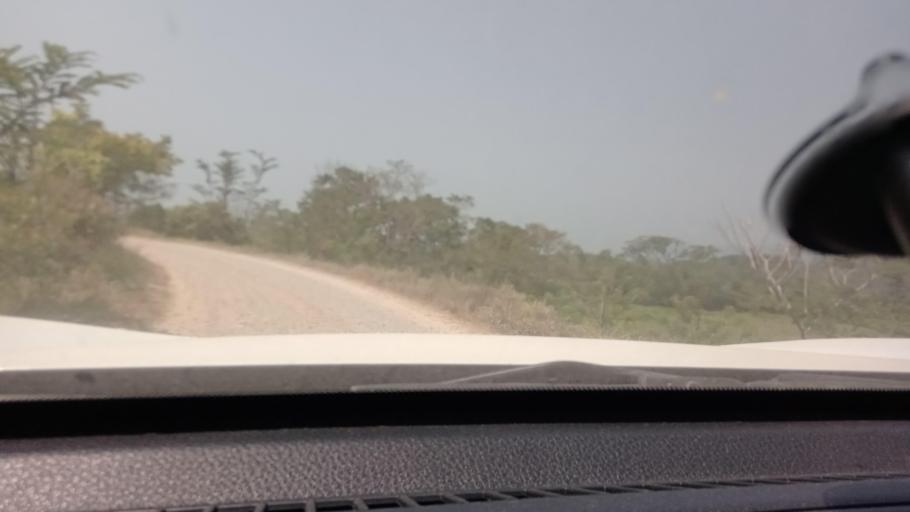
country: MX
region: Tabasco
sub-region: Huimanguillo
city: Francisco Rueda
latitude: 17.5132
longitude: -93.8969
